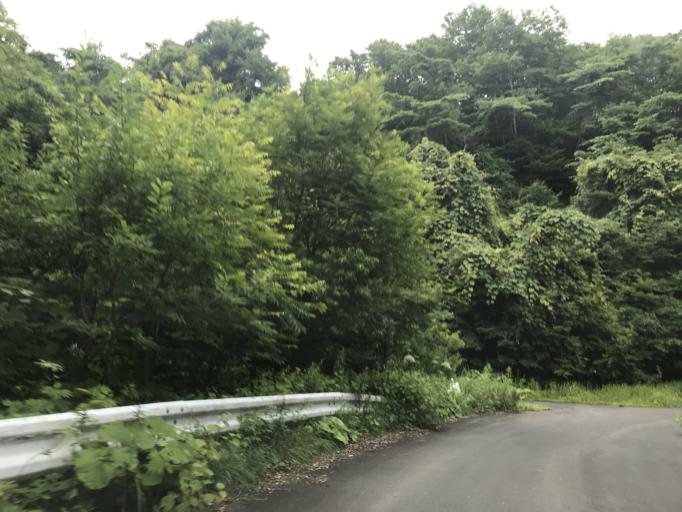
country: JP
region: Iwate
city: Ichinoseki
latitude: 38.9555
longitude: 140.8815
